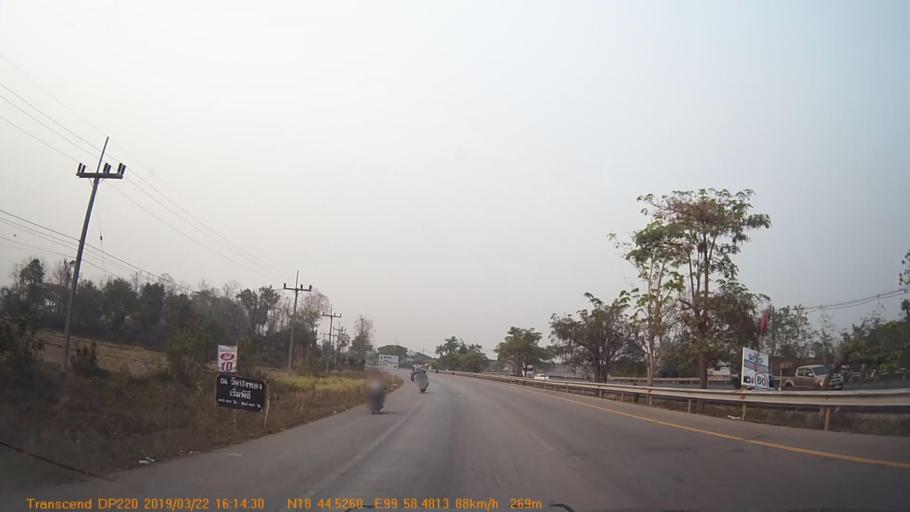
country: TH
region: Lampang
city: Ngao
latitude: 18.7425
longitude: 99.9747
